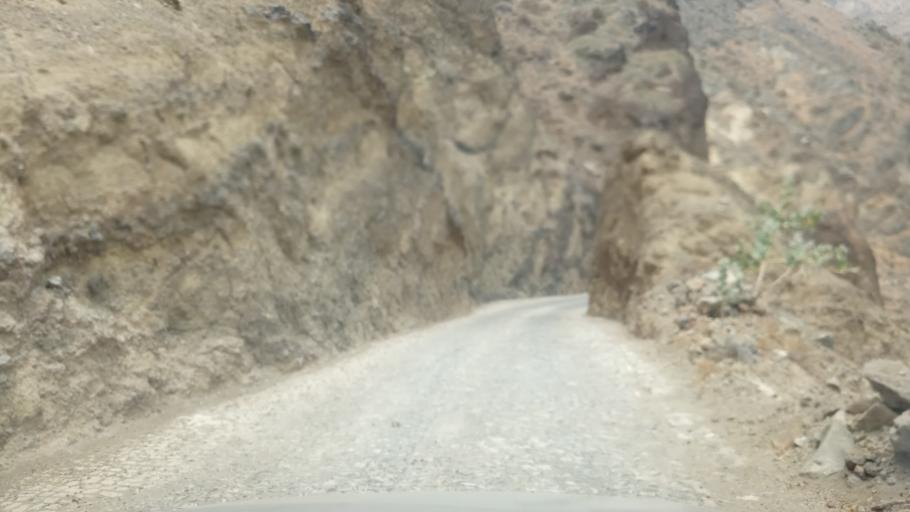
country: CV
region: Brava
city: Vila Nova Sintra
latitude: 14.8751
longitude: -24.7322
